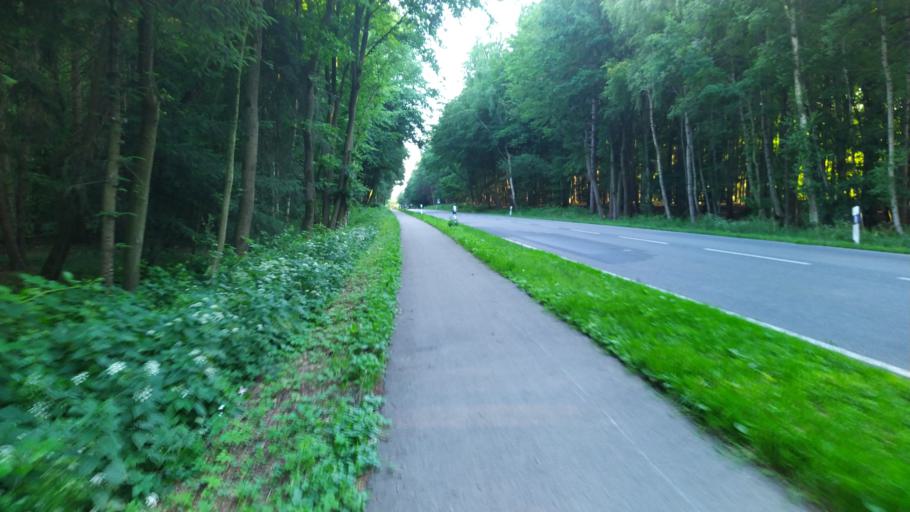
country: DE
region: Lower Saxony
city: Alfstedt
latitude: 53.5410
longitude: 9.0574
